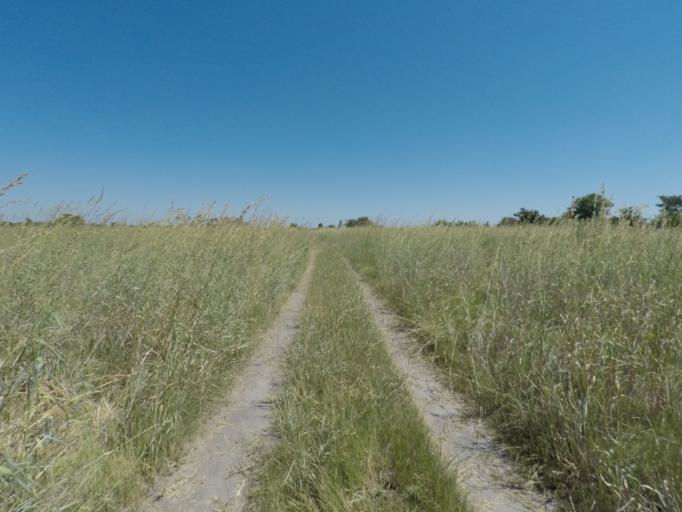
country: BW
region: North West
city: Maun
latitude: -19.4863
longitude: 23.5291
